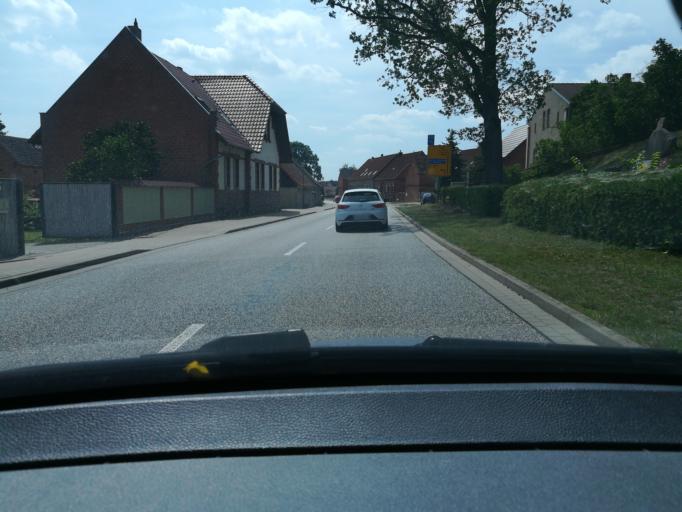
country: DE
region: Brandenburg
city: Wittstock
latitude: 53.0714
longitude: 12.4740
